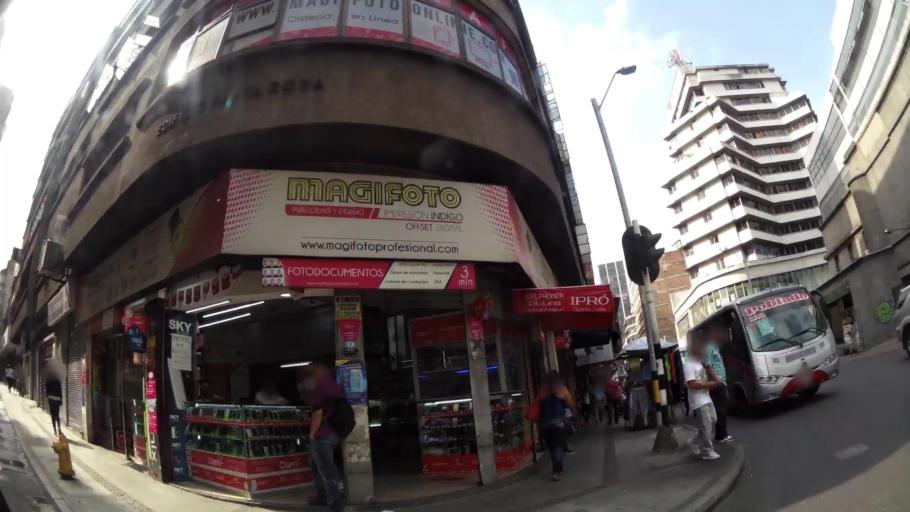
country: CO
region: Antioquia
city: Medellin
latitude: 6.2524
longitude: -75.5667
